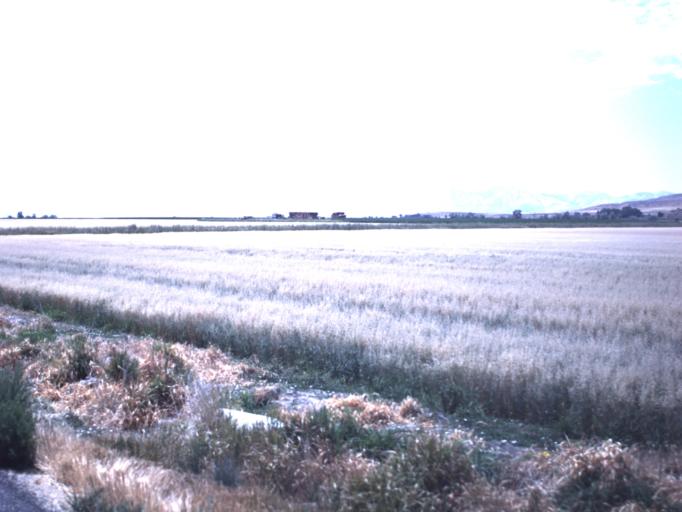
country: US
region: Utah
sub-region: Box Elder County
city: Tremonton
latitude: 41.6445
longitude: -112.3142
